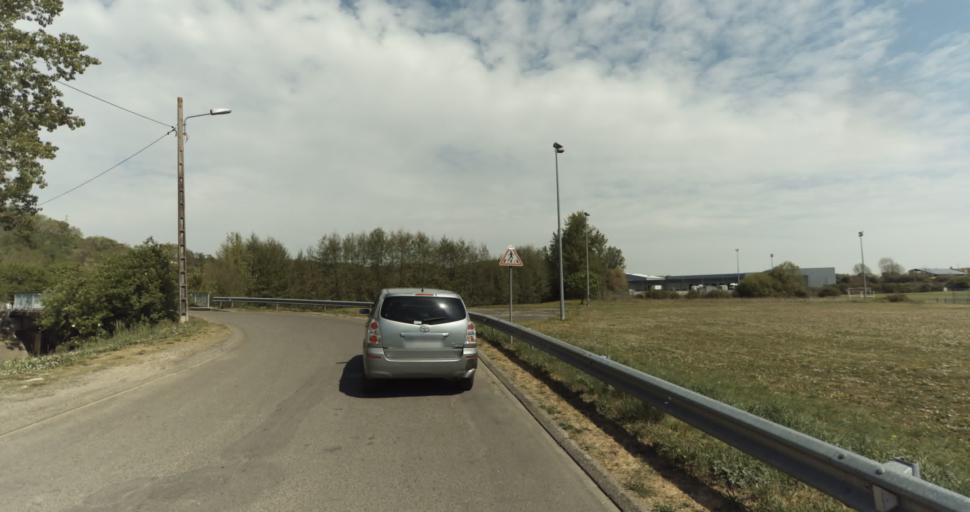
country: FR
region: Aquitaine
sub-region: Departement du Lot-et-Garonne
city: Agen
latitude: 44.2154
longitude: 0.6494
